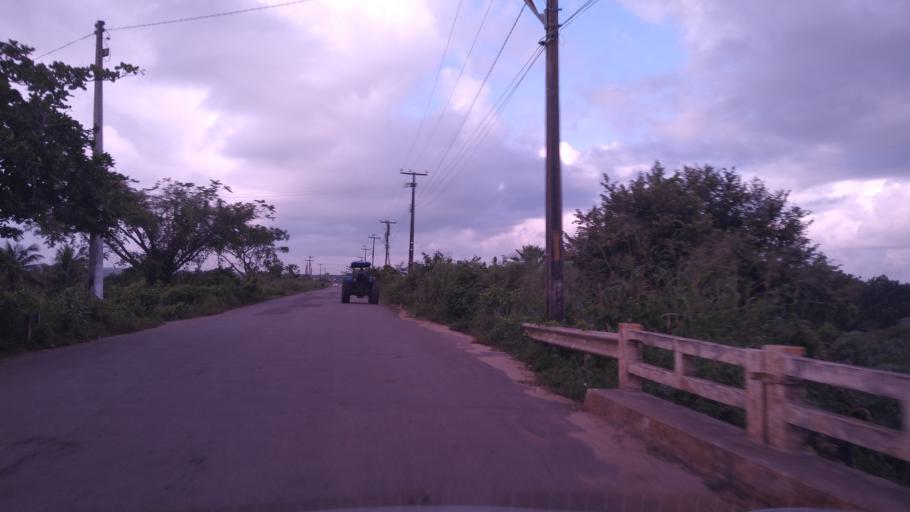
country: BR
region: Ceara
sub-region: Chorozinho
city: Chorozinho
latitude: -4.3040
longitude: -38.4978
